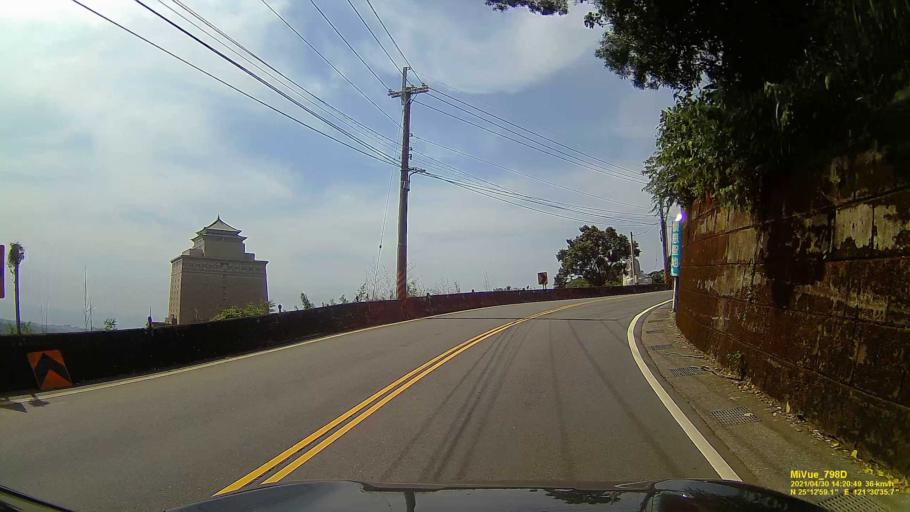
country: TW
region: Taipei
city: Taipei
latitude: 25.2166
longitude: 121.5098
